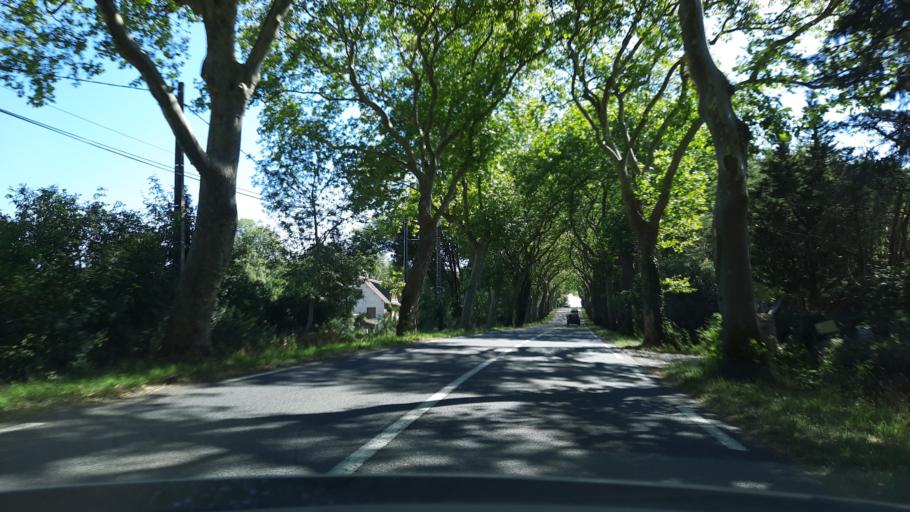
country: FR
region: Midi-Pyrenees
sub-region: Departement de l'Aveyron
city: Villefranche-de-Rouergue
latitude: 44.3232
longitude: 1.8979
